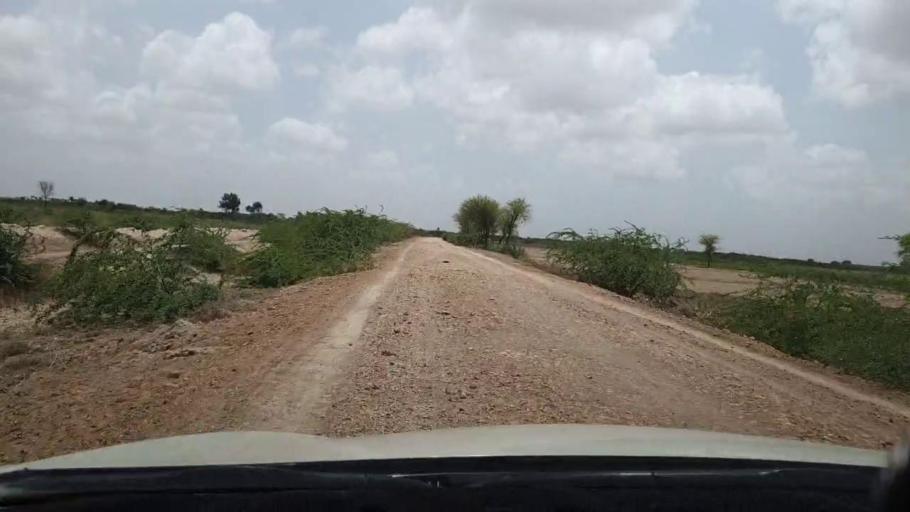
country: PK
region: Sindh
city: Kadhan
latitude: 24.3887
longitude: 68.9339
